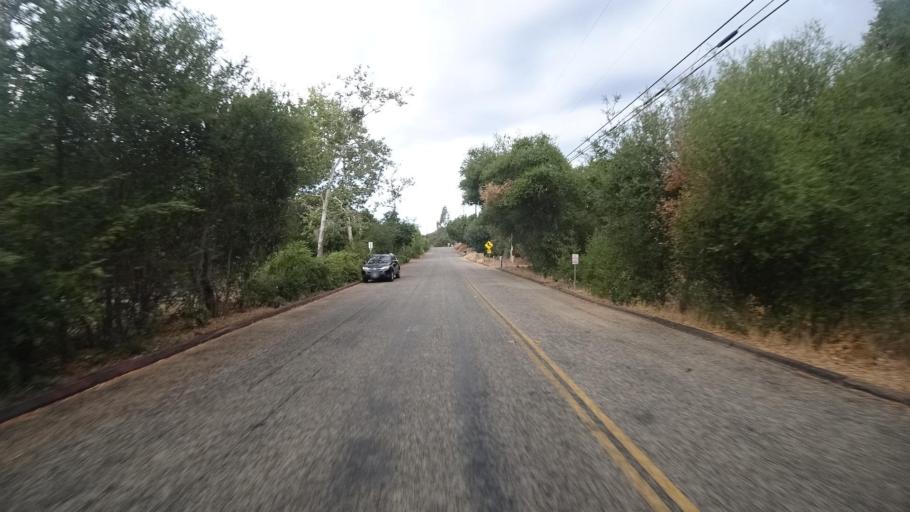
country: US
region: California
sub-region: San Diego County
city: Ramona
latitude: 32.9997
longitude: -116.9380
